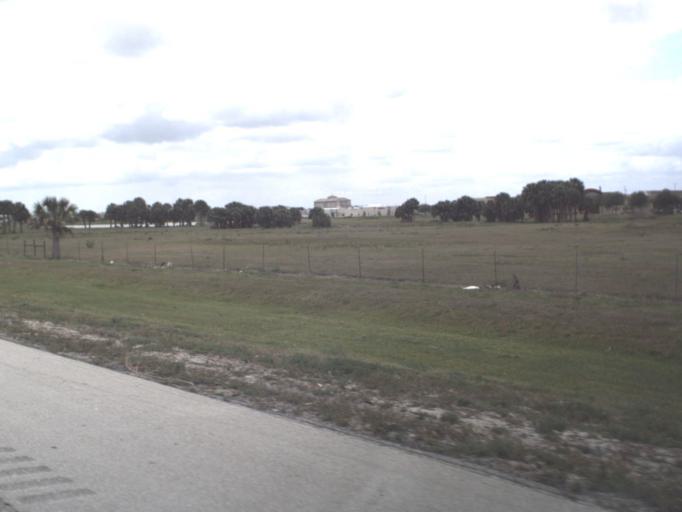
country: US
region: Florida
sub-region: Brevard County
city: Rockledge
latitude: 28.2430
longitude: -80.7224
